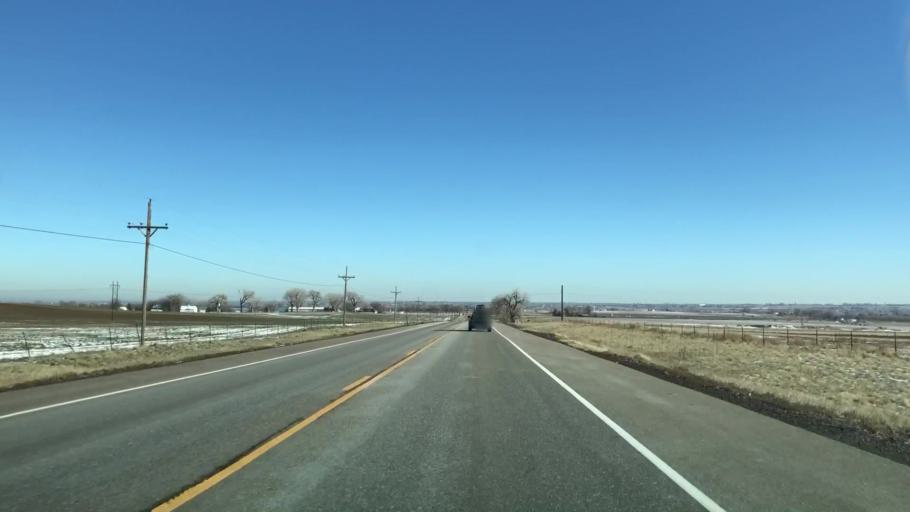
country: US
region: Colorado
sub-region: Boulder County
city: Niwot
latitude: 40.0880
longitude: -105.1180
